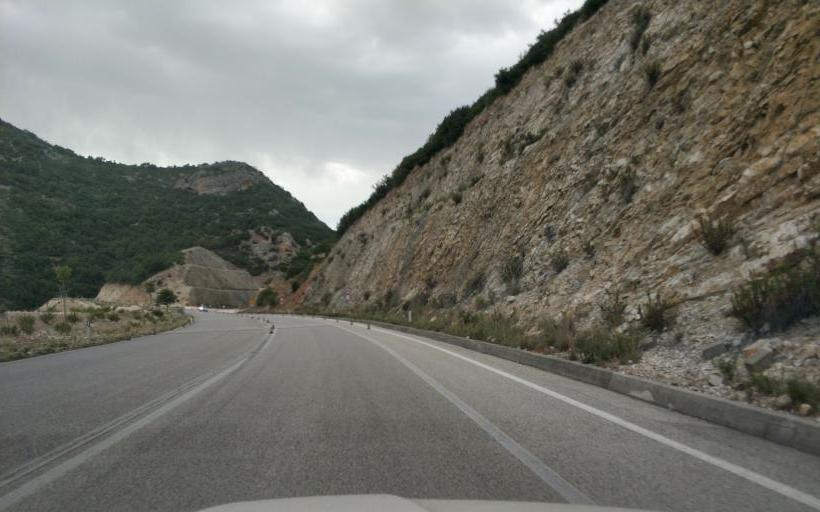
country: AL
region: Fier
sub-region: Rrethi i Mallakastres
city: Kute
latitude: 40.5086
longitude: 19.7560
